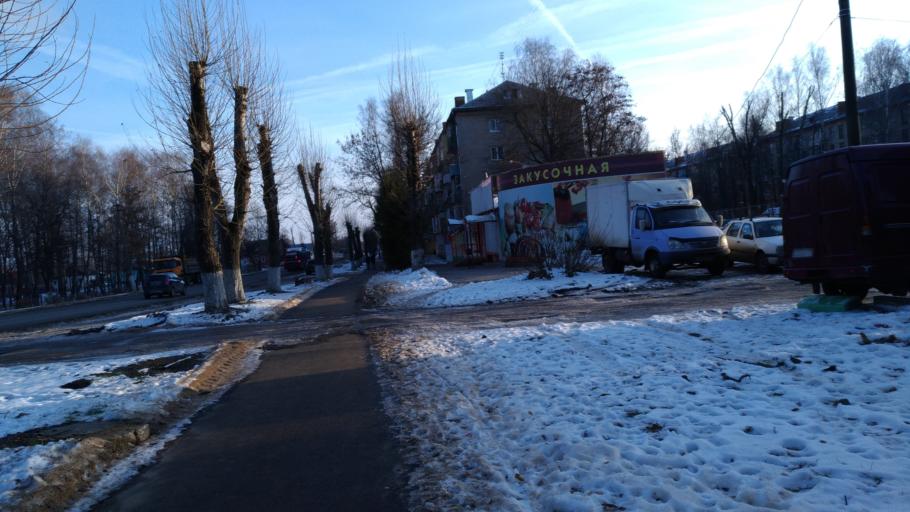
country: RU
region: Tula
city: Tula
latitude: 54.1926
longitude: 37.6942
